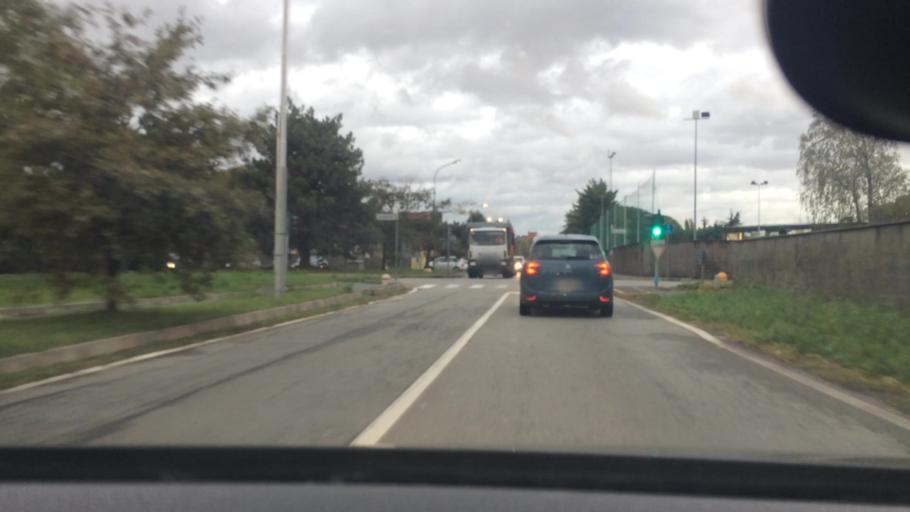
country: IT
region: Lombardy
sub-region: Citta metropolitana di Milano
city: Nerviano
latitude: 45.5444
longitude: 8.9732
